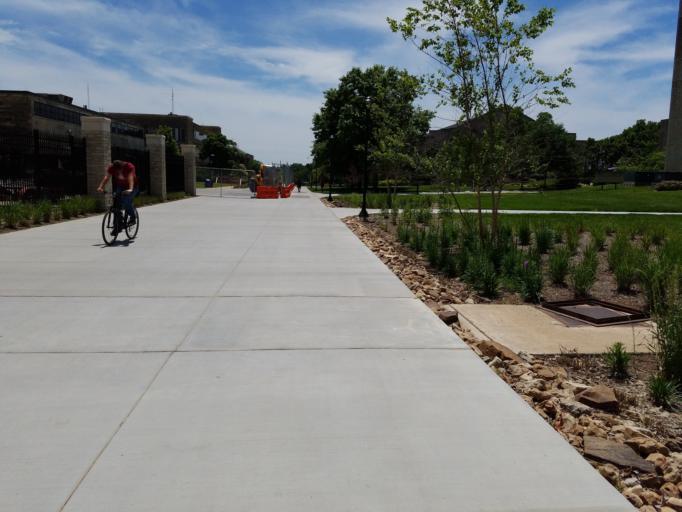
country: US
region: Kansas
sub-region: Riley County
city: Manhattan
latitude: 39.1907
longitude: -96.5834
